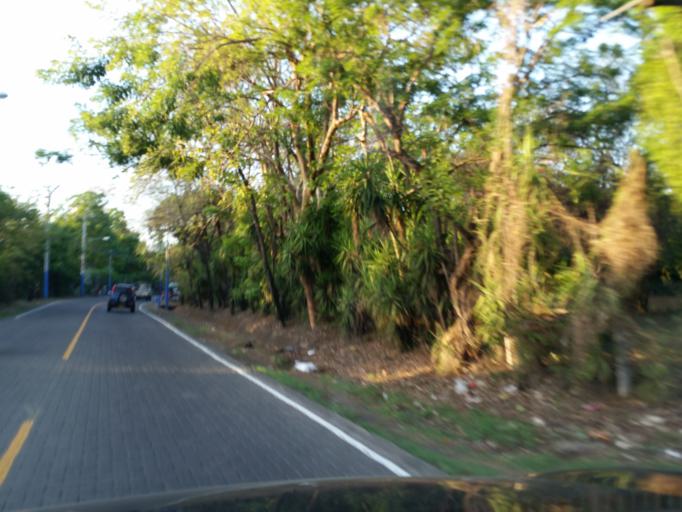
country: NI
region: Masaya
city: Ticuantepe
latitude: 12.0376
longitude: -86.2047
